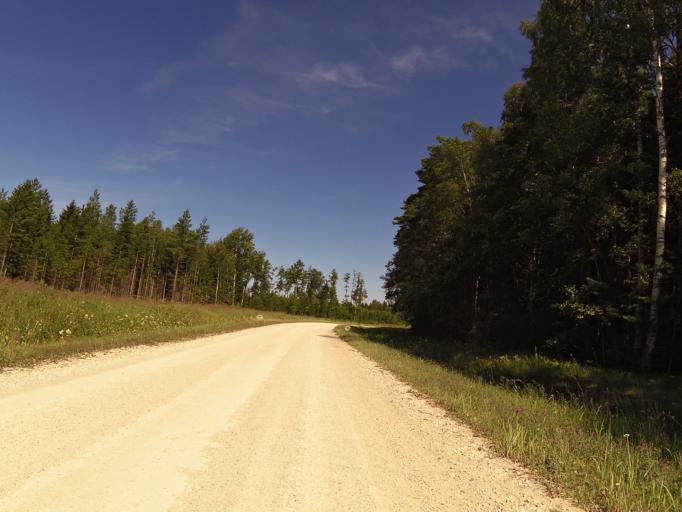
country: EE
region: Hiiumaa
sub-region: Kaerdla linn
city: Kardla
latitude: 58.9253
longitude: 22.3679
